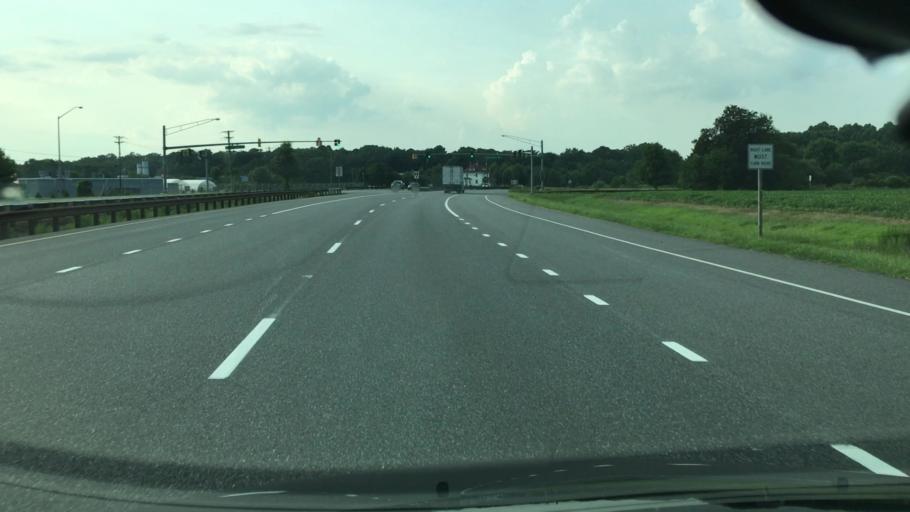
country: US
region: Maryland
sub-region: Worcester County
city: Ocean Pines
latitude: 38.4043
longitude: -75.2114
